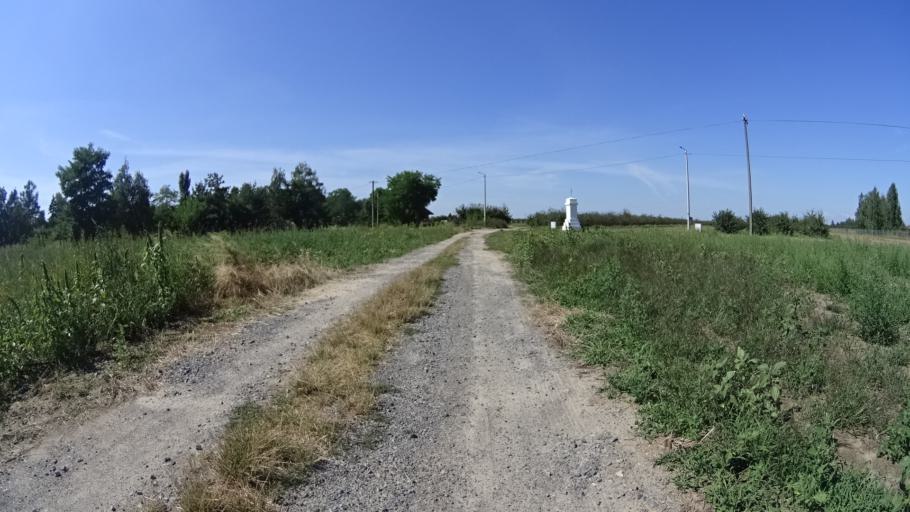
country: PL
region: Masovian Voivodeship
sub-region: Powiat bialobrzeski
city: Bialobrzegi
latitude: 51.6706
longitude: 20.9075
